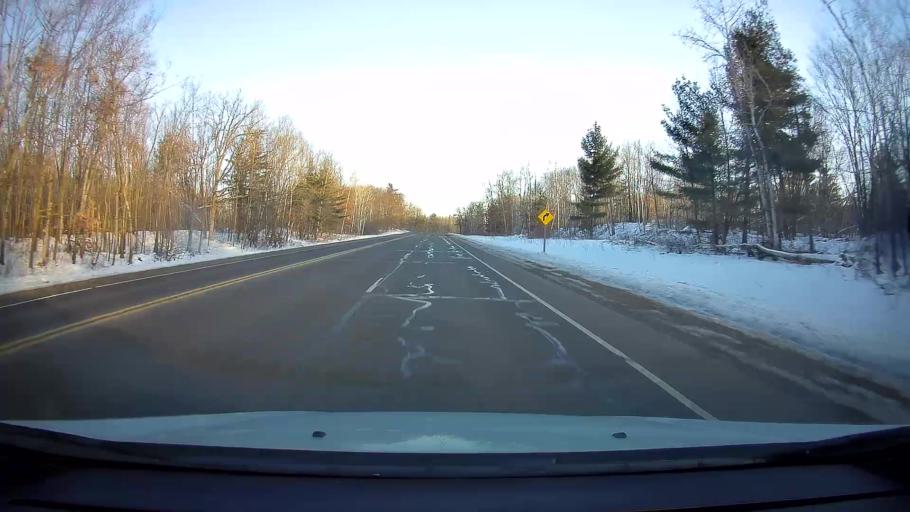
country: US
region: Wisconsin
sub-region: Barron County
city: Turtle Lake
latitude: 45.4324
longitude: -92.1296
